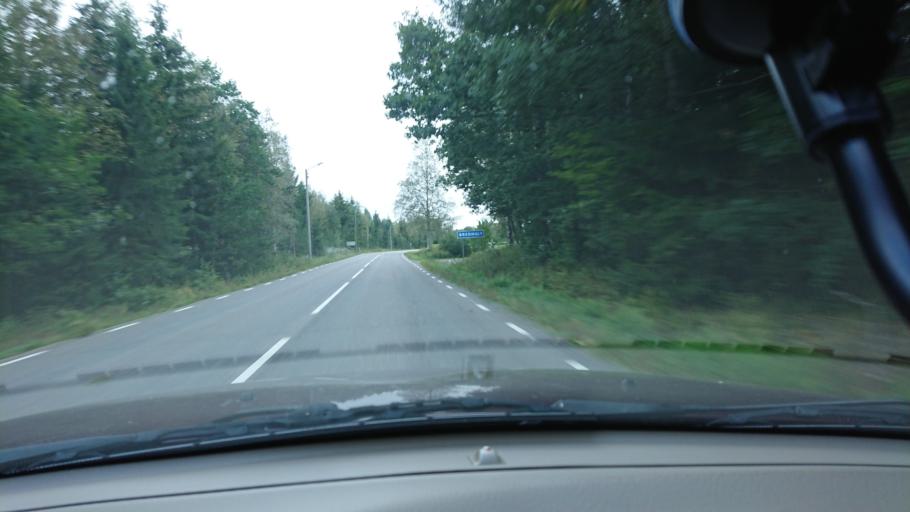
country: SE
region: Kronoberg
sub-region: Vaxjo Kommun
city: Lammhult
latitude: 57.0899
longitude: 14.6482
